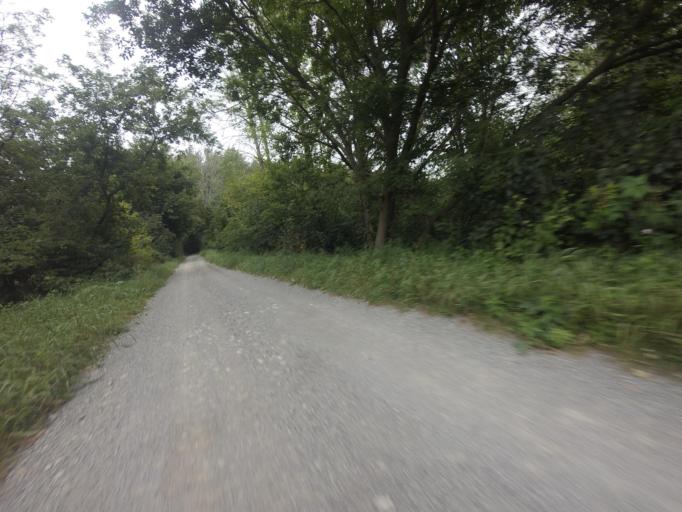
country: CA
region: Ontario
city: Omemee
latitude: 44.3901
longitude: -78.7571
